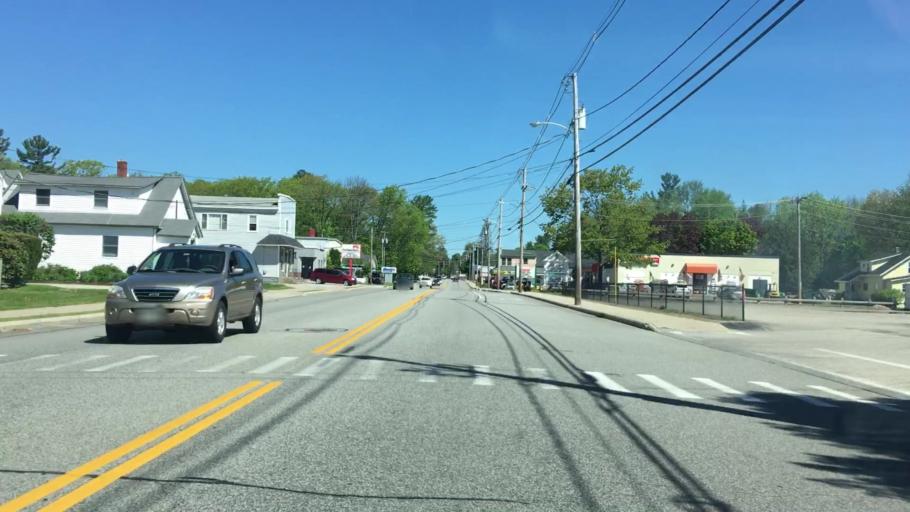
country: US
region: Maine
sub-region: York County
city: Springvale
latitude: 43.4531
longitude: -70.7888
